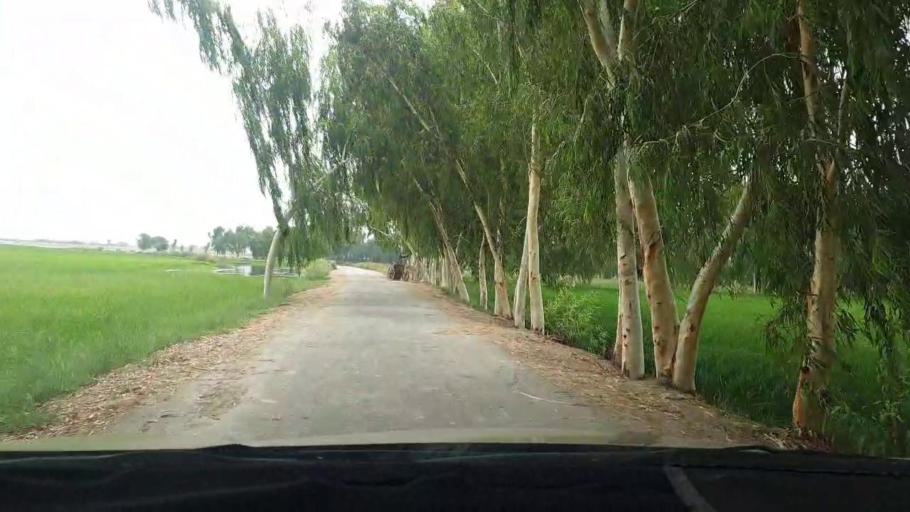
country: PK
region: Sindh
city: Naudero
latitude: 27.6224
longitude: 68.3274
